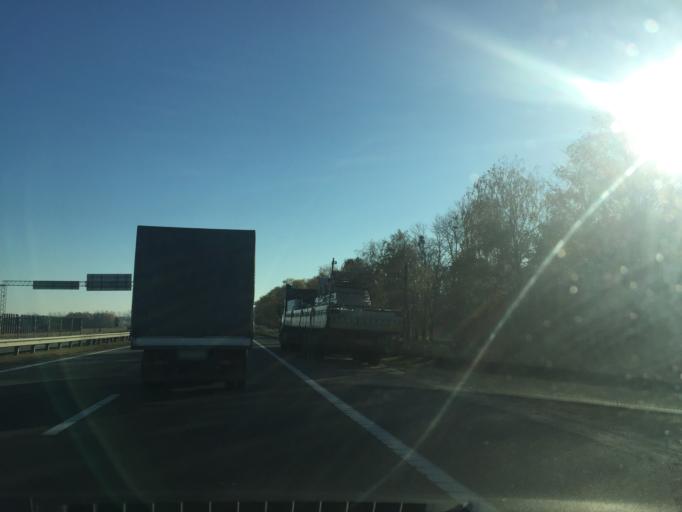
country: BY
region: Minsk
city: Smilavichy
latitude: 53.7593
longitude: 28.0203
